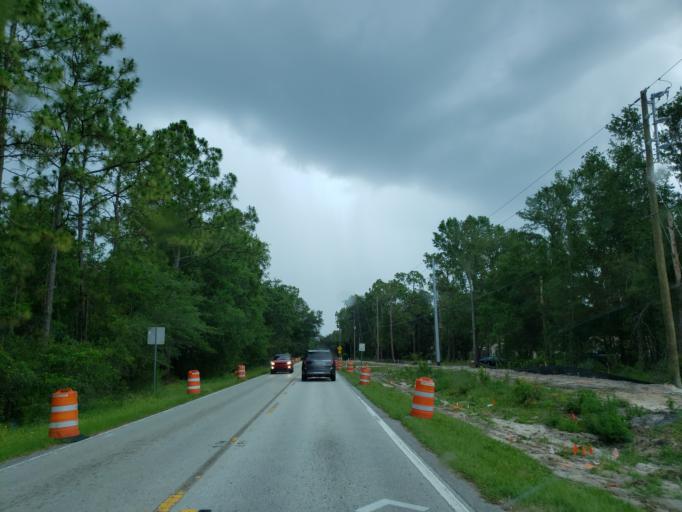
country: US
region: Florida
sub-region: Pasco County
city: Wesley Chapel
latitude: 28.2497
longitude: -82.3543
